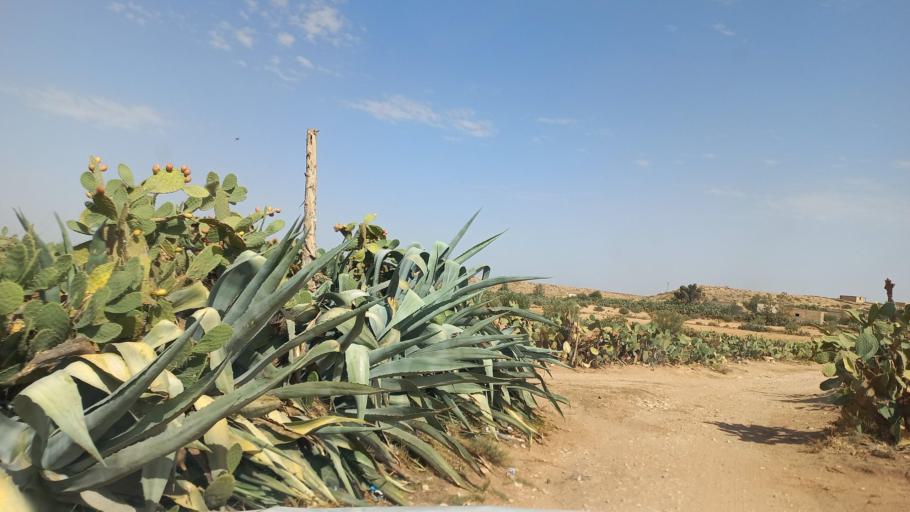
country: TN
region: Al Qasrayn
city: Kasserine
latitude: 35.2790
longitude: 8.9674
